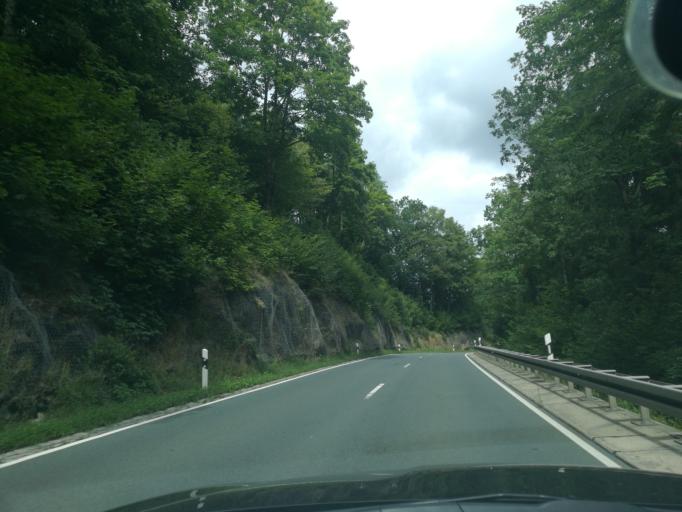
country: DE
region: Saxony
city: Adorf
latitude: 50.3477
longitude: 12.2354
